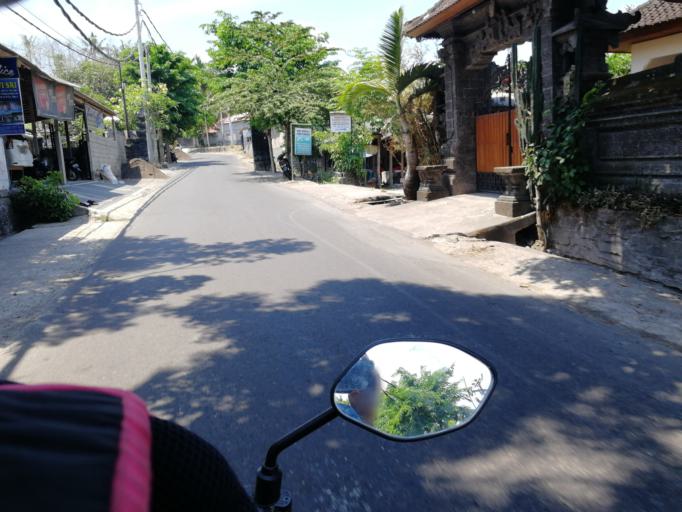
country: ID
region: Bali
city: Banjar Timbrah
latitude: -8.4756
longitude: 115.5960
